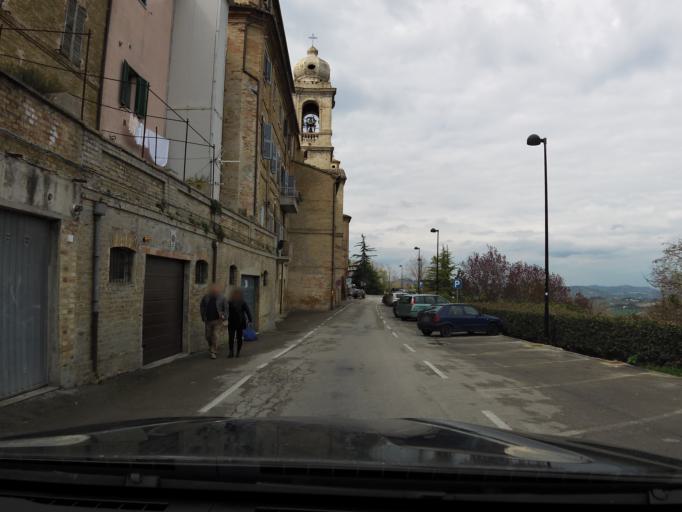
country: IT
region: The Marches
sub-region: Provincia di Ancona
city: Castelfidardo
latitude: 43.4647
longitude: 13.5473
